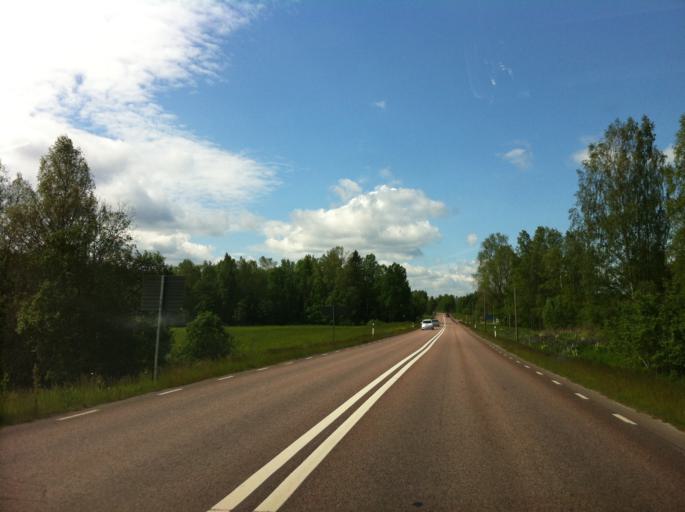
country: SE
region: Vaermland
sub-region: Karlstads Kommun
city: Valberg
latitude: 59.3792
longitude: 13.1626
